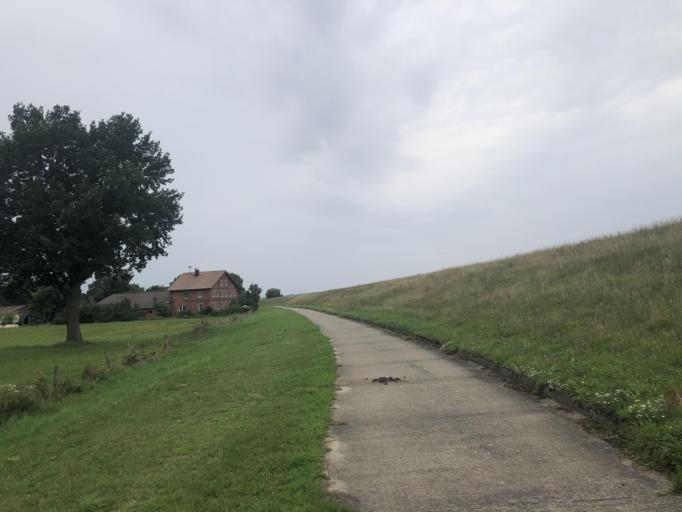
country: DE
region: Schleswig-Holstein
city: Lanze
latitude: 53.3688
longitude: 10.6388
